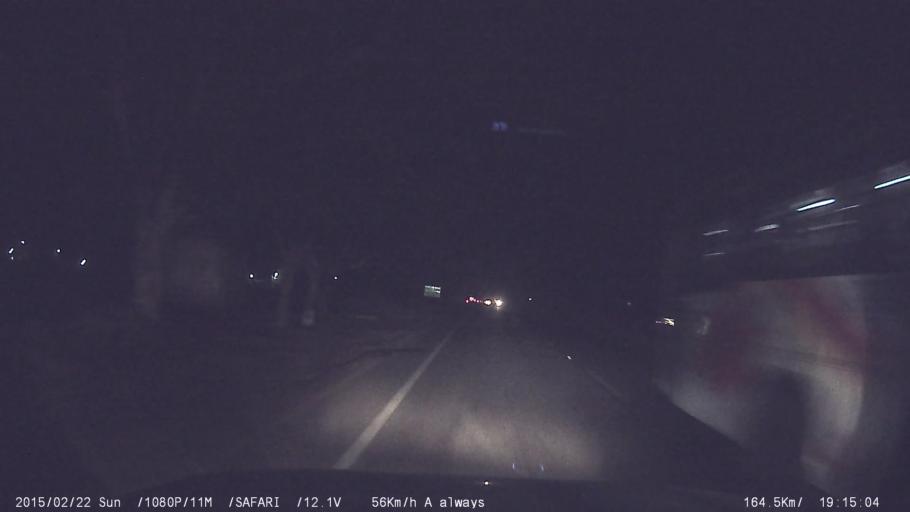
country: IN
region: Tamil Nadu
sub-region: Theni
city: Periyakulam
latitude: 10.0877
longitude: 77.5245
